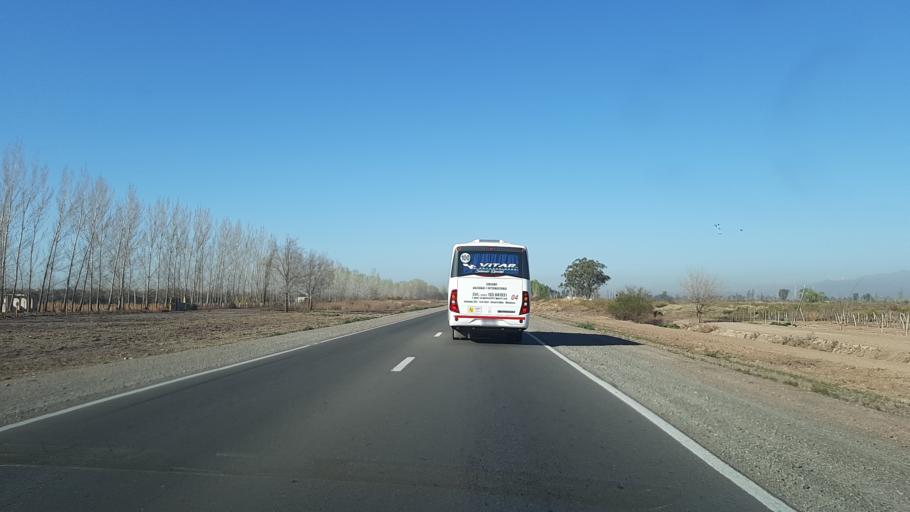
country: AR
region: Mendoza
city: General Lavalle
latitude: -32.6924
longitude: -68.6681
